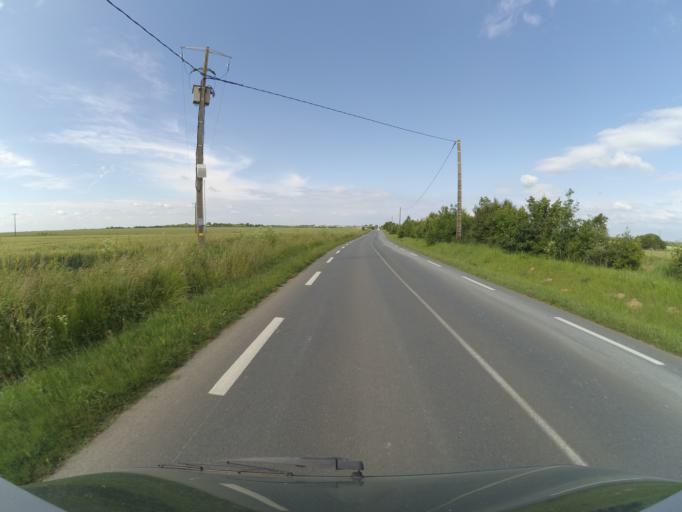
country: FR
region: Poitou-Charentes
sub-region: Departement de la Charente-Maritime
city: Saint-Xandre
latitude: 46.2246
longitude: -1.0840
